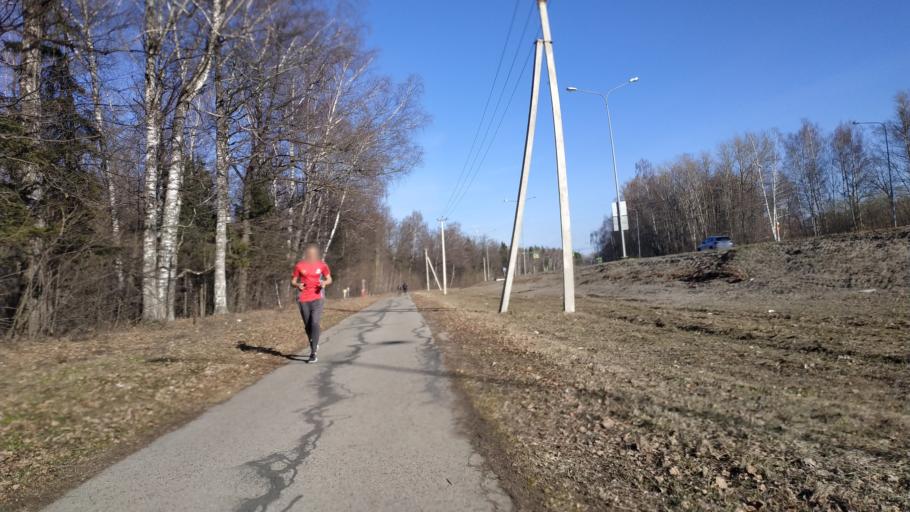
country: RU
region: Chuvashia
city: Ishley
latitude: 56.1330
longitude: 47.1077
